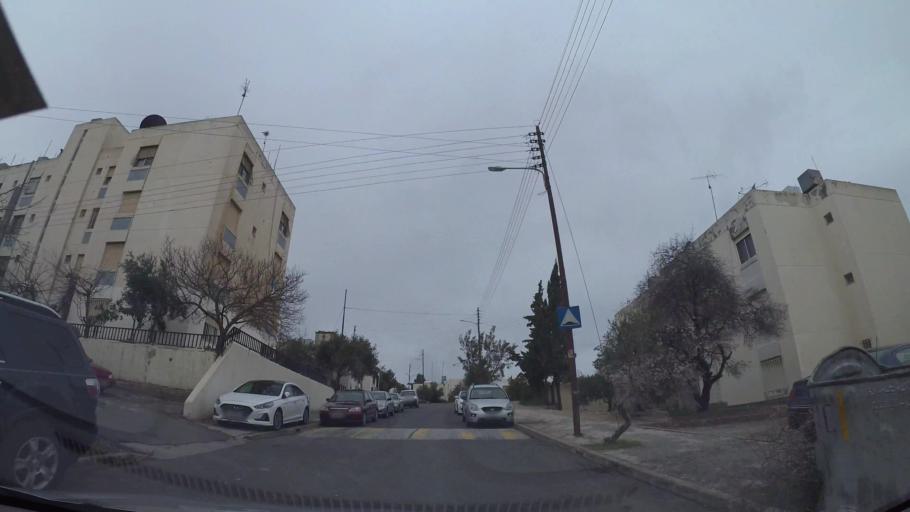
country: JO
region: Amman
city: Al Jubayhah
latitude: 32.0549
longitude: 35.8820
